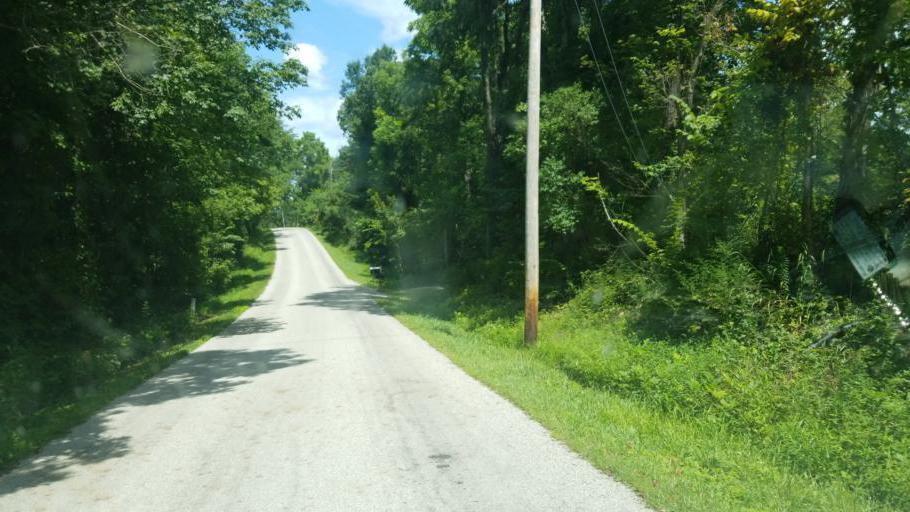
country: US
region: Ohio
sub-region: Delaware County
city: Sunbury
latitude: 40.2815
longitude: -82.8308
